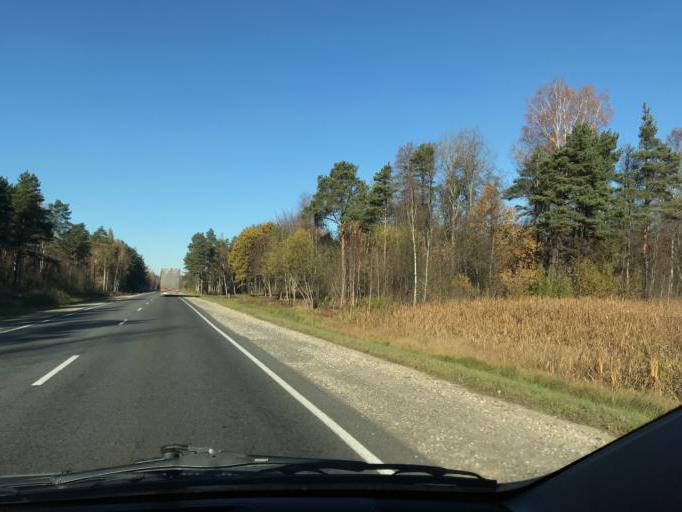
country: BY
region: Vitebsk
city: Polatsk
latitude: 55.5104
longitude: 28.7429
